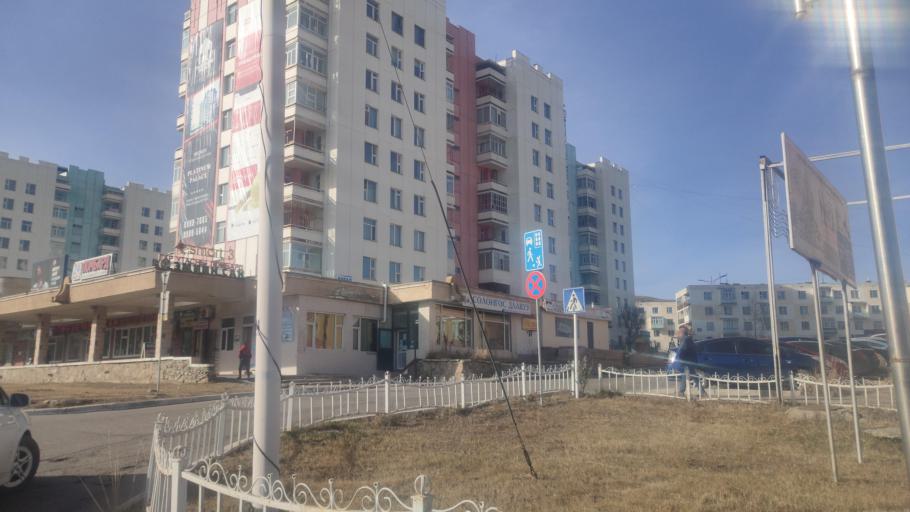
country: MN
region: Orhon
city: Erdenet
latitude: 49.0298
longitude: 104.0521
